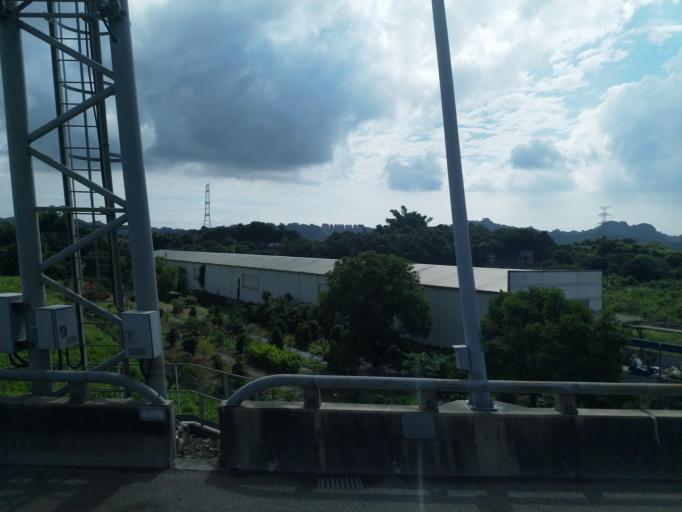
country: TW
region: Taiwan
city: Fengshan
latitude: 22.7502
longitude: 120.3645
